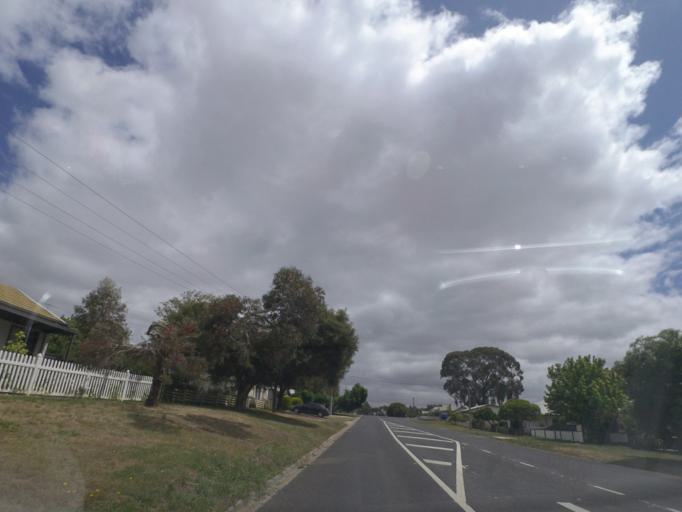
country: AU
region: Victoria
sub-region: Whittlesea
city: Whittlesea
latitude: -37.2095
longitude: 145.0457
